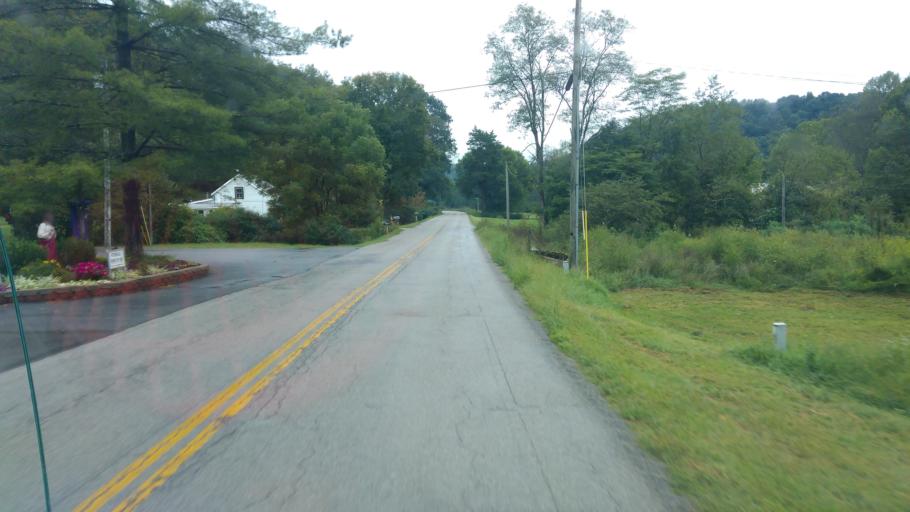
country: US
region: Kentucky
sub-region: Fleming County
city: Flemingsburg
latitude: 38.4473
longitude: -83.5044
